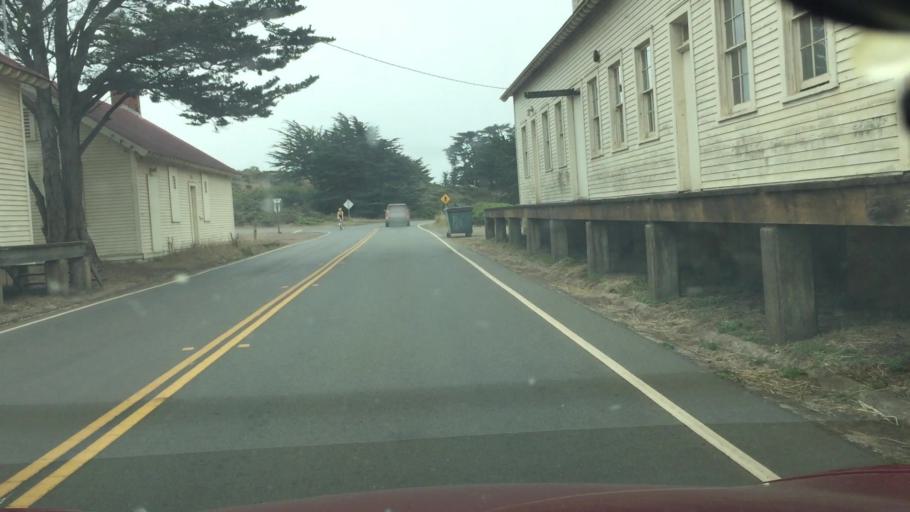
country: US
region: California
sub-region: Marin County
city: Marin City
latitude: 37.8272
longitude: -122.5264
